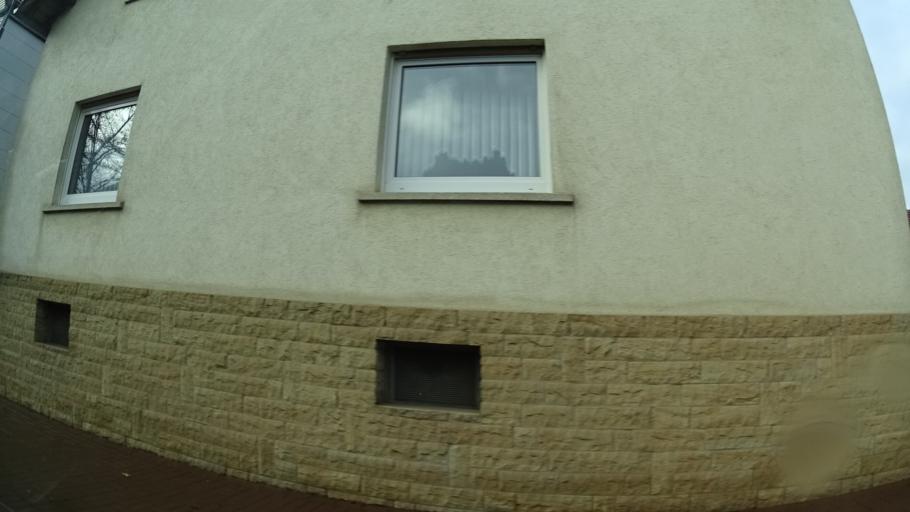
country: DE
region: Hesse
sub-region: Regierungsbezirk Kassel
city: Neuhof
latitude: 50.4512
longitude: 9.6211
